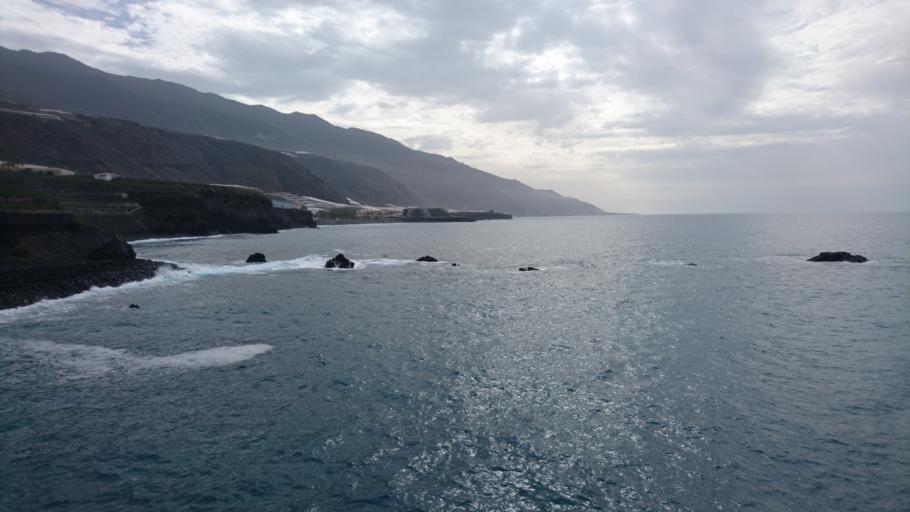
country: ES
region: Canary Islands
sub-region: Provincia de Santa Cruz de Tenerife
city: Tazacorte
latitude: 28.5911
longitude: -17.9179
